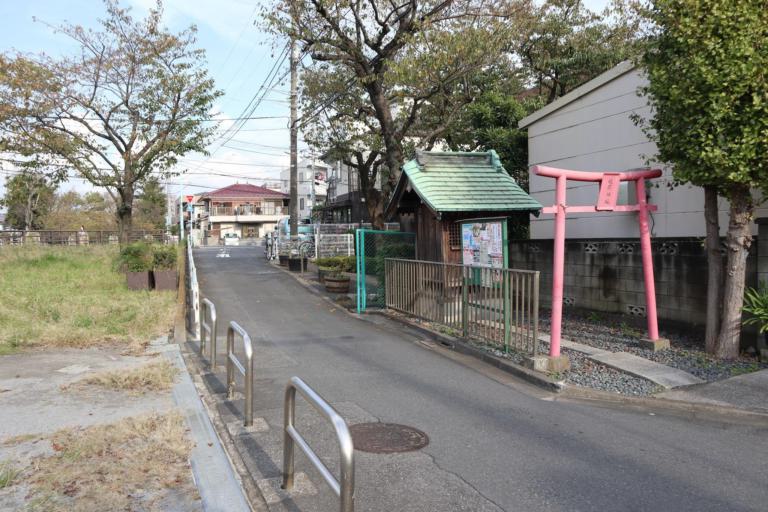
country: JP
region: Tokyo
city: Urayasu
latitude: 35.6748
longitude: 139.8727
